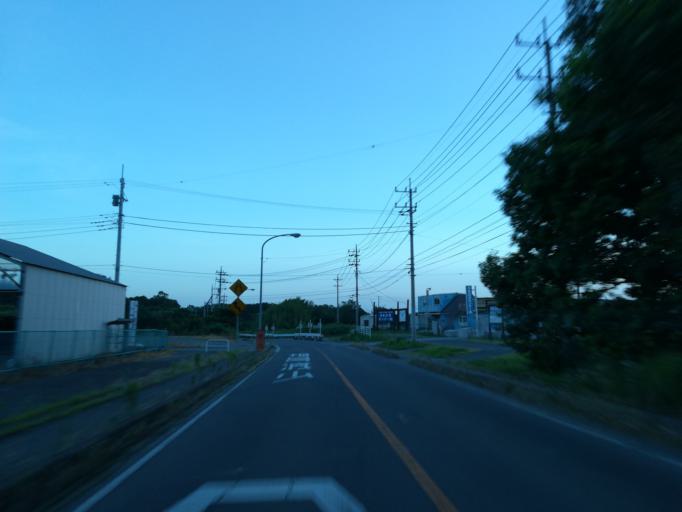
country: JP
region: Ibaraki
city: Iwase
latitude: 36.3172
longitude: 140.0667
